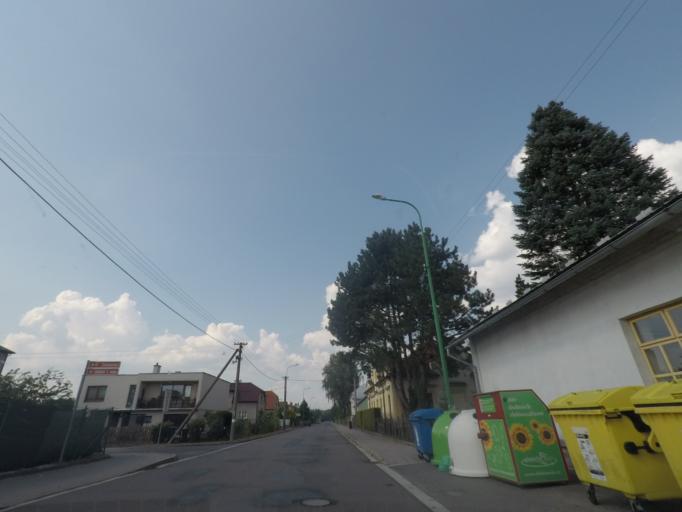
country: CZ
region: Pardubicky
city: Horni Jeleni
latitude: 50.0516
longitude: 16.0838
